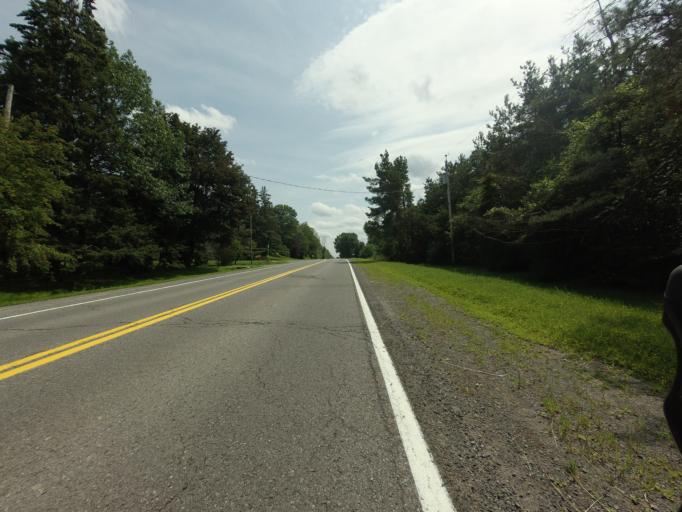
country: CA
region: Ontario
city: Ottawa
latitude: 45.2810
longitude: -75.6289
